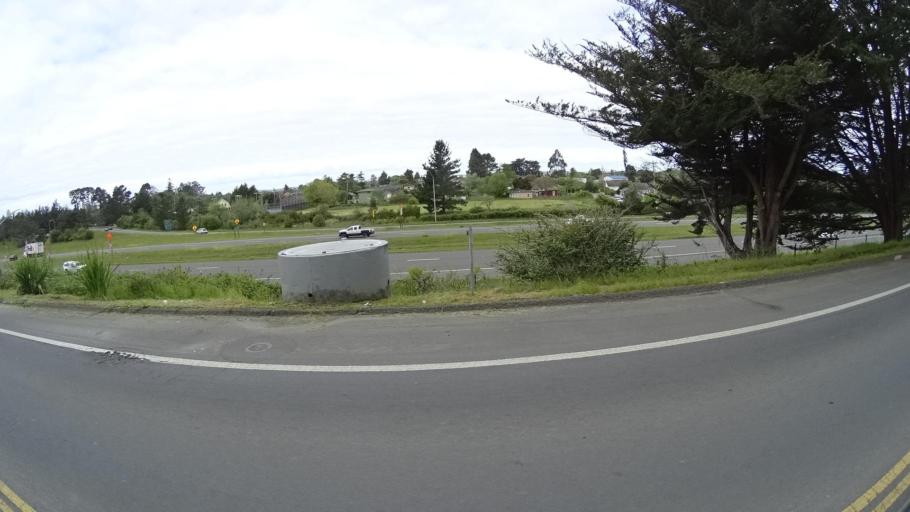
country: US
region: California
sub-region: Humboldt County
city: Arcata
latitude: 40.8809
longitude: -124.0801
